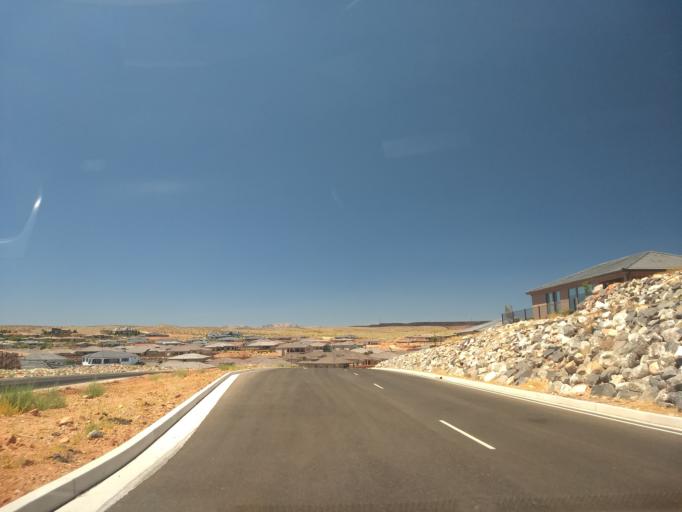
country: US
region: Utah
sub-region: Washington County
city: Washington
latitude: 37.1593
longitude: -113.5246
